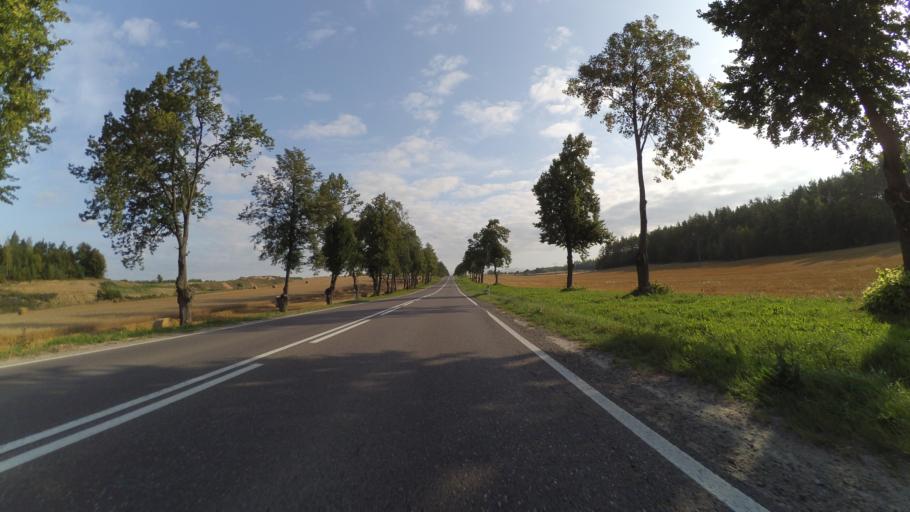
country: PL
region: Podlasie
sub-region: Powiat sokolski
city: Sokolka
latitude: 53.3540
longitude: 23.4137
